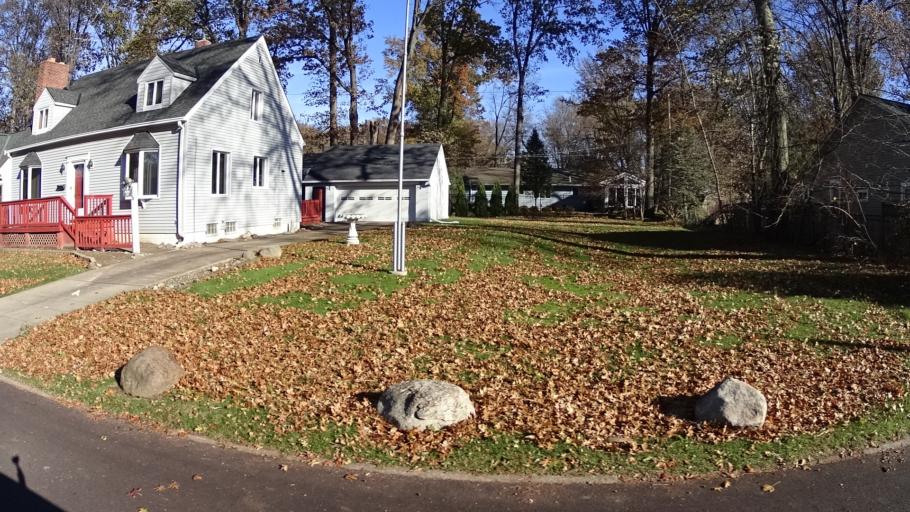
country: US
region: Ohio
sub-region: Lorain County
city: Avon Lake
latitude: 41.5088
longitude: -82.0025
